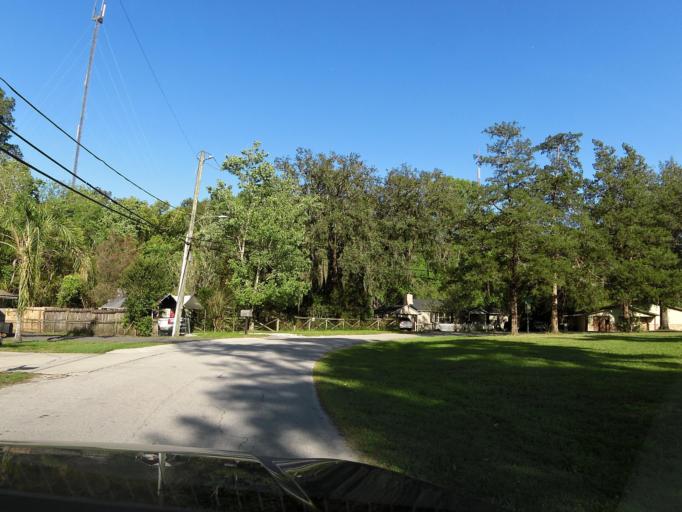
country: US
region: Florida
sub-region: Duval County
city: Jacksonville
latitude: 30.2789
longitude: -81.5743
